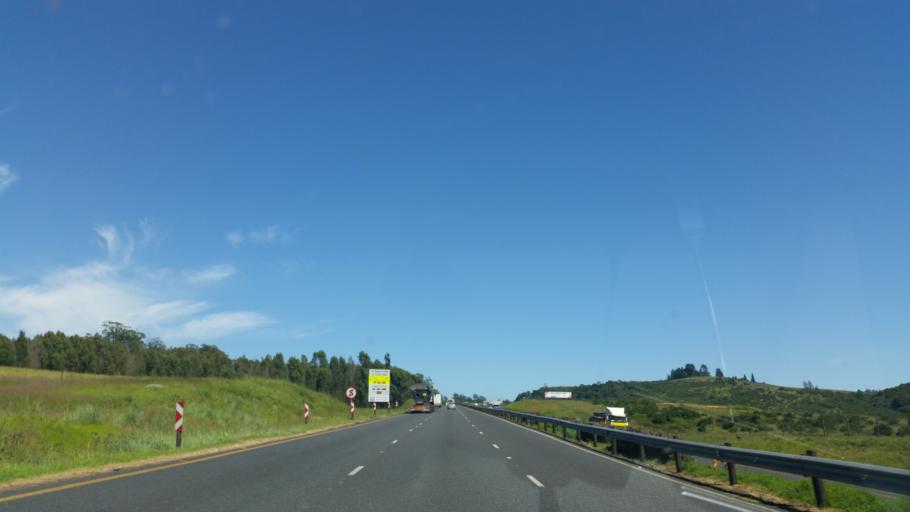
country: ZA
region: KwaZulu-Natal
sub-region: uMgungundlovu District Municipality
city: Mooirivier
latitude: -29.3315
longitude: 30.0634
